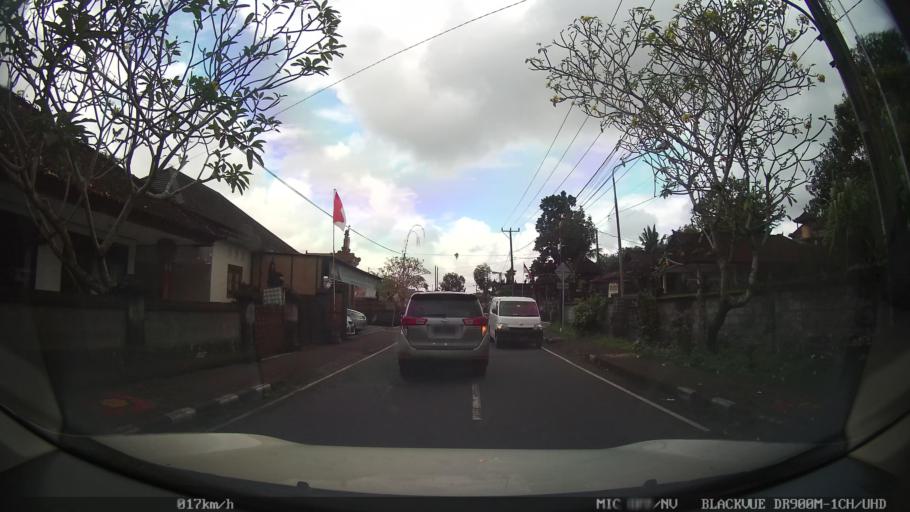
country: ID
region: Bali
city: Banjar Sempidi
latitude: -8.5298
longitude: 115.2010
